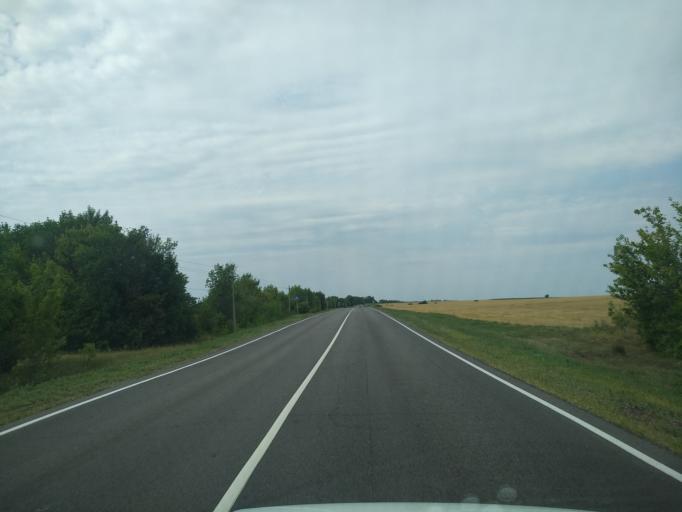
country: RU
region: Voronezj
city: Pereleshinskiy
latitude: 51.8322
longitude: 40.2898
